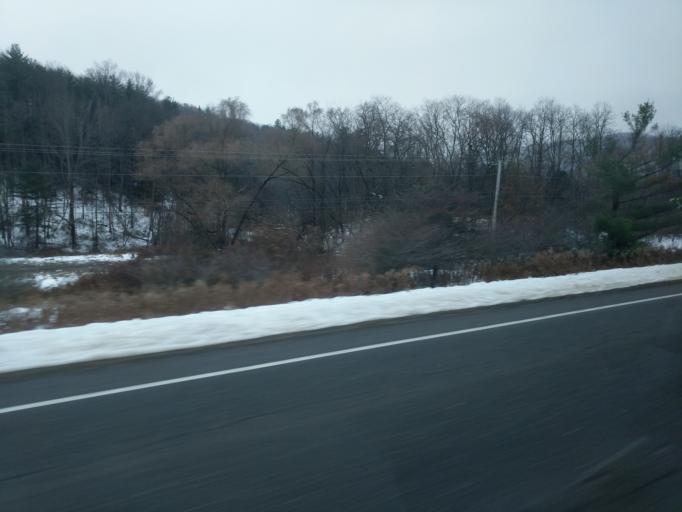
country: US
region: Pennsylvania
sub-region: Tioga County
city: Wellsboro
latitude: 41.8542
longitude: -77.2422
